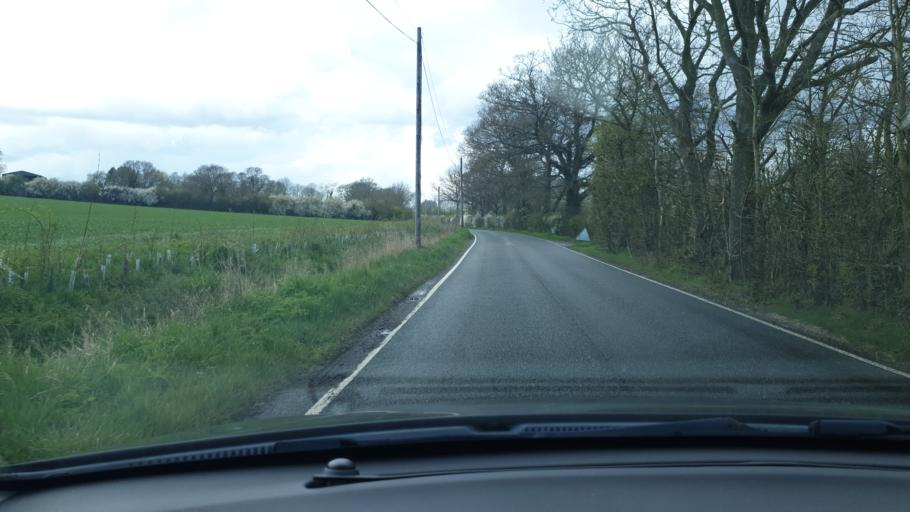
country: GB
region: England
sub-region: Essex
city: Little Clacton
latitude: 51.9103
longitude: 1.1669
